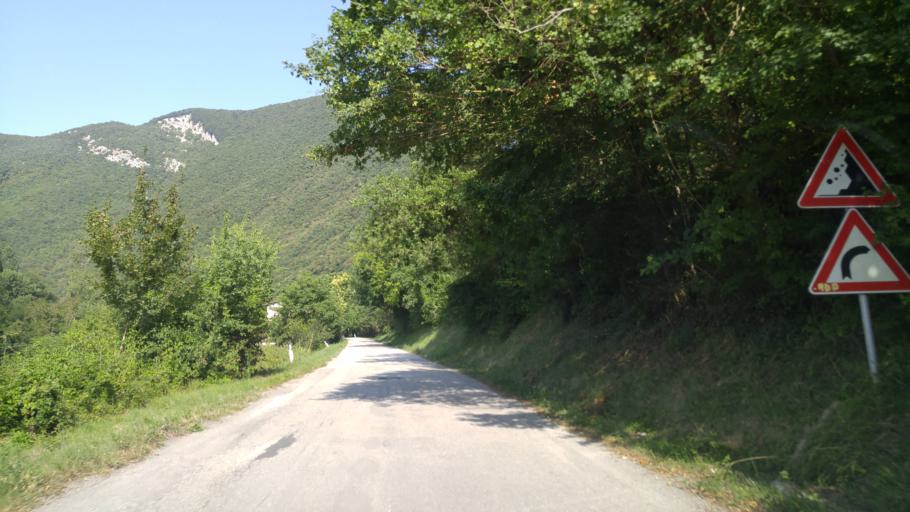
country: IT
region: The Marches
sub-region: Provincia di Pesaro e Urbino
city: Acqualagna
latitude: 43.6343
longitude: 12.7098
